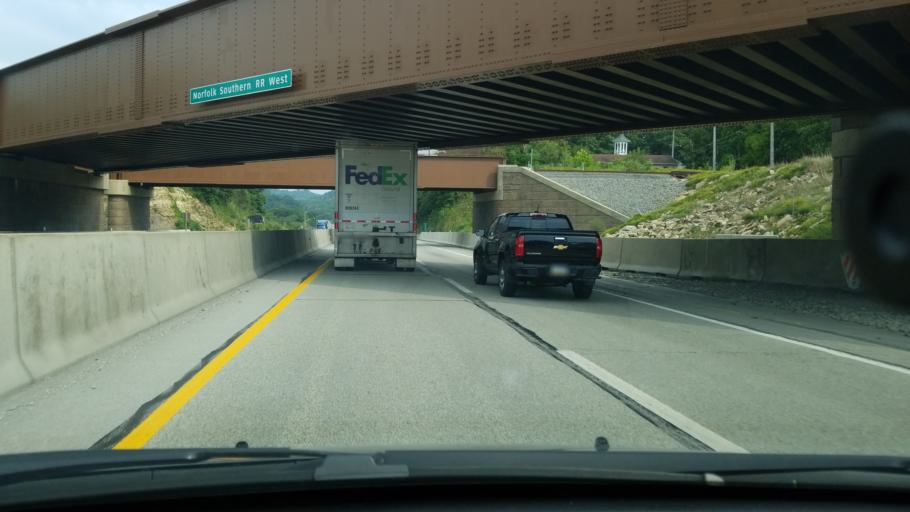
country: US
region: Pennsylvania
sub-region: Beaver County
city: Big Beaver
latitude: 40.8157
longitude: -80.3282
